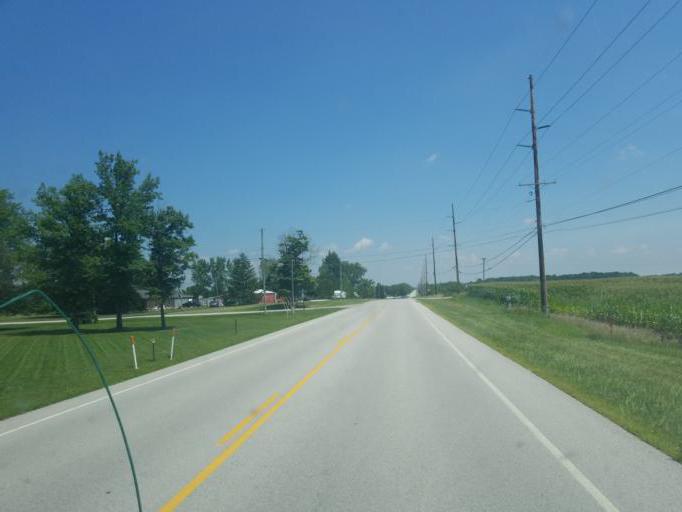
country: US
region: Ohio
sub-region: Auglaize County
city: Saint Marys
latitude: 40.5534
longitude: -84.3183
